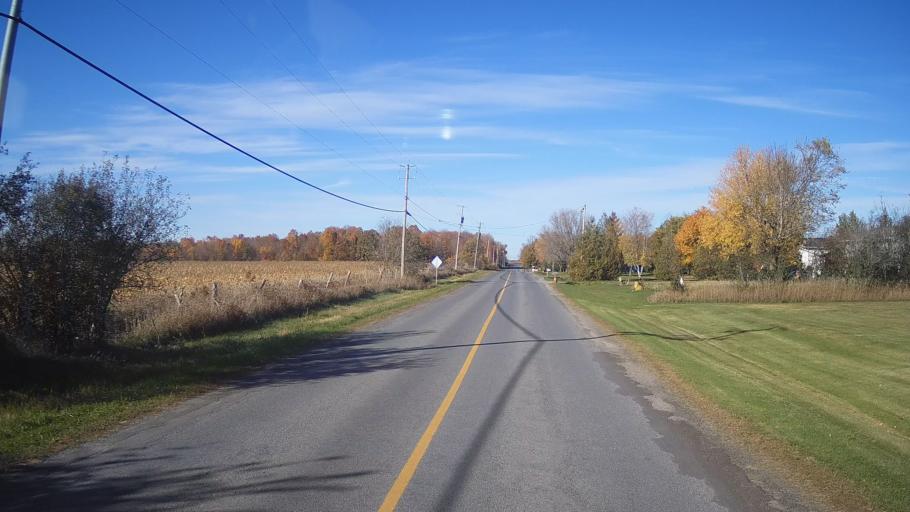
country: CA
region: Ontario
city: Kingston
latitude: 44.4095
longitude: -76.5274
